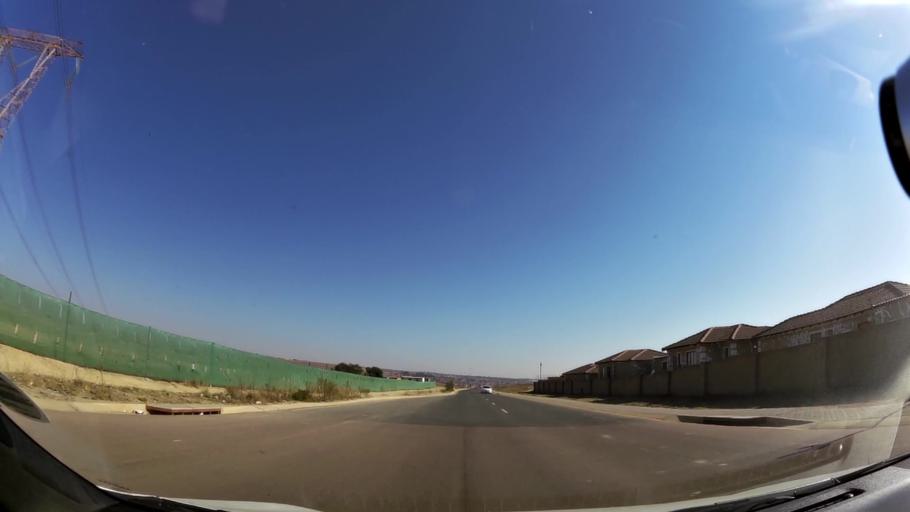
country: ZA
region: Gauteng
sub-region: City of Tshwane Metropolitan Municipality
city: Centurion
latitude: -25.9119
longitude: 28.1293
